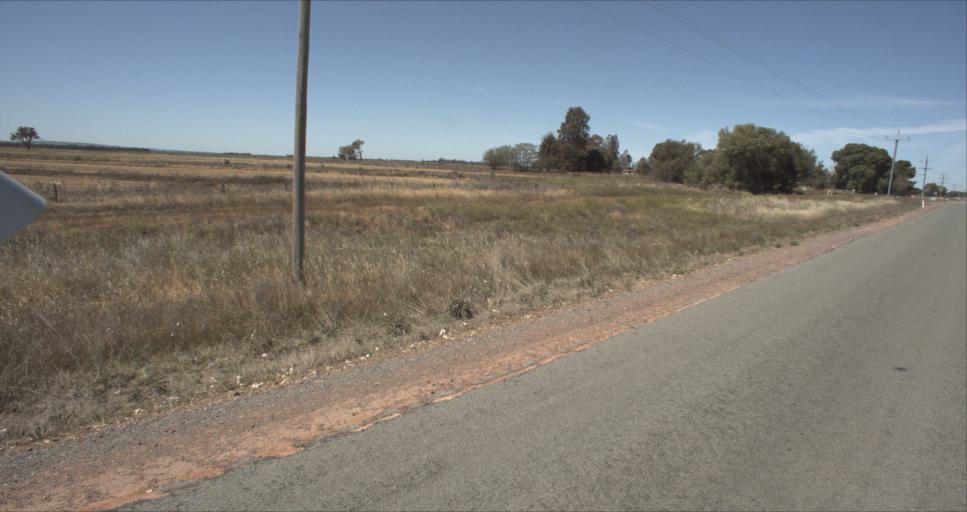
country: AU
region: New South Wales
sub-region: Leeton
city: Leeton
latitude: -34.4394
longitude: 146.2981
